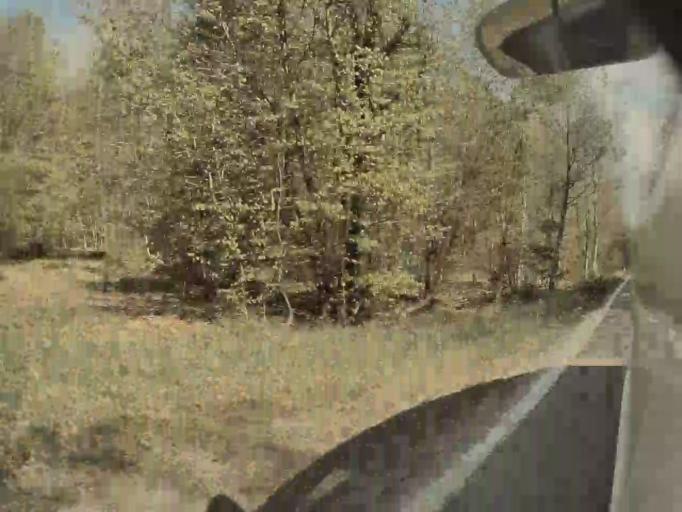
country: BE
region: Wallonia
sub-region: Province du Luxembourg
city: Tellin
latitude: 50.0224
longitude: 5.2027
